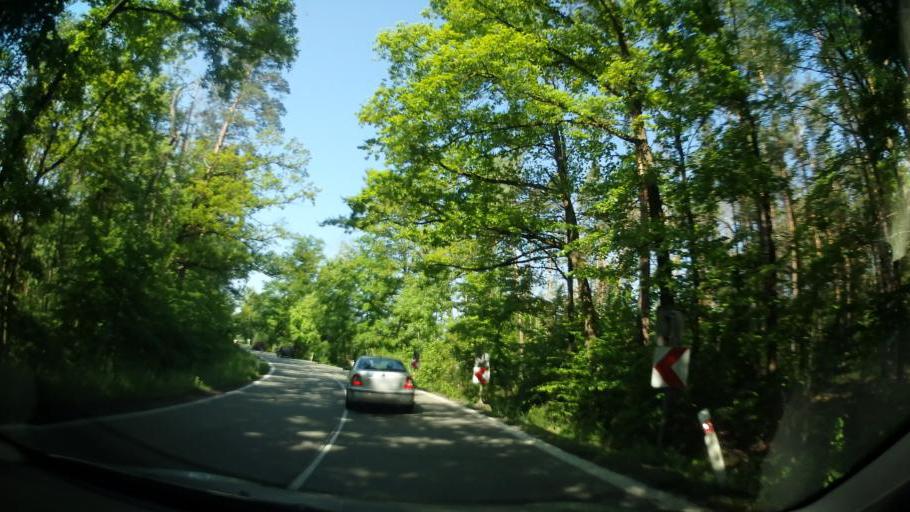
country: CZ
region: South Moravian
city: Zastavka
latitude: 49.1849
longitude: 16.3347
